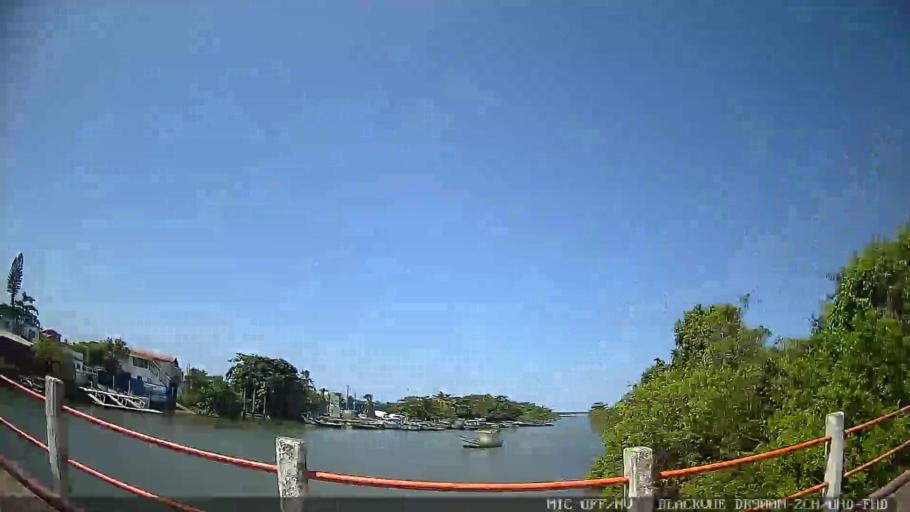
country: BR
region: Sao Paulo
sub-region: Peruibe
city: Peruibe
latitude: -24.3298
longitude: -47.0045
